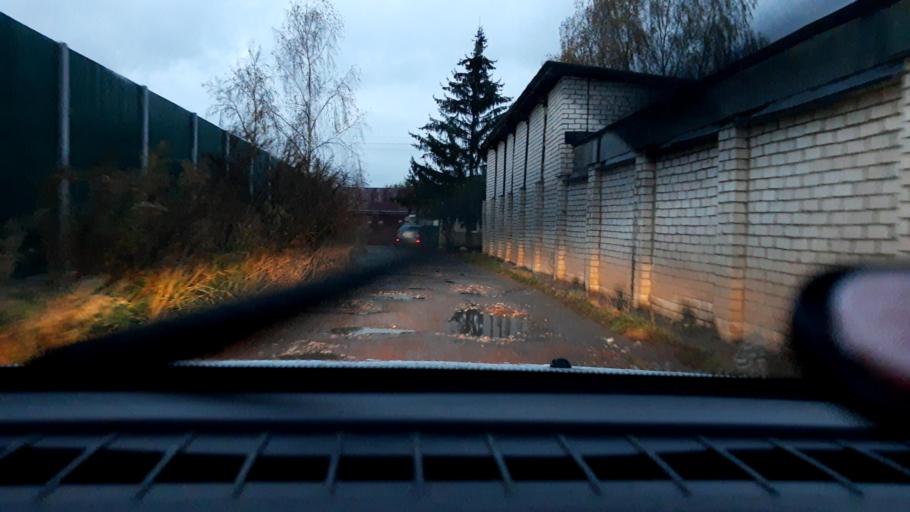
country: RU
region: Nizjnij Novgorod
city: Afonino
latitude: 56.2249
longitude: 44.1019
